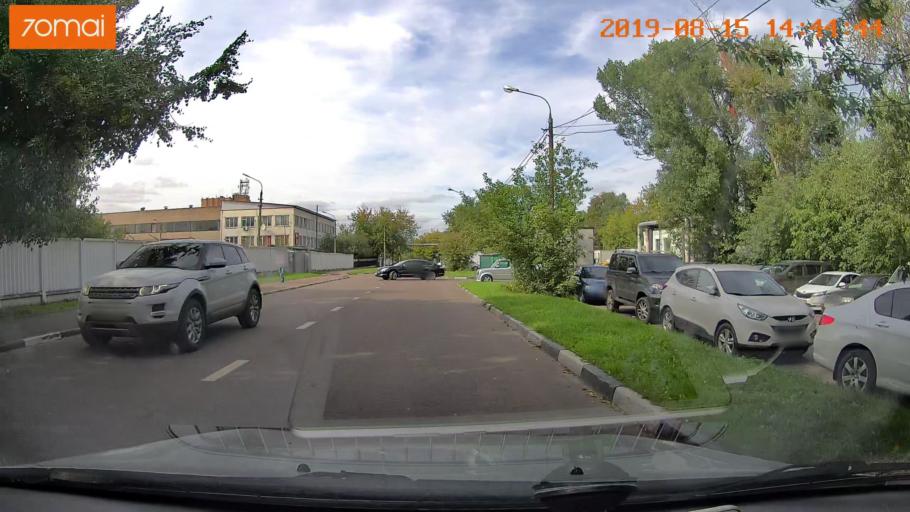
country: RU
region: Moskovskaya
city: Lyubertsy
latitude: 55.6703
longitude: 37.9029
